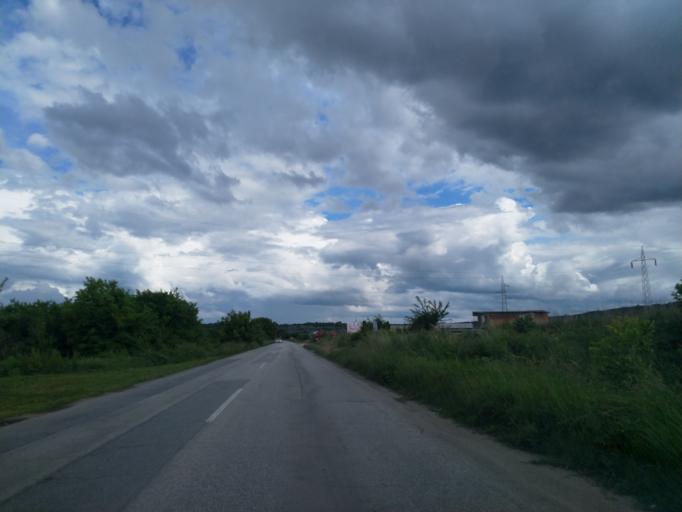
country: RS
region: Central Serbia
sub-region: Pomoravski Okrug
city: Jagodina
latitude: 43.9605
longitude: 21.2840
